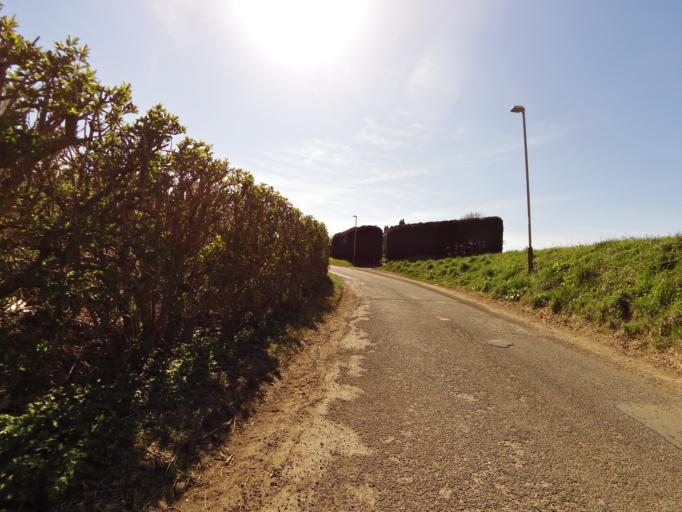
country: GB
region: Scotland
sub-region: Angus
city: Montrose
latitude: 56.6997
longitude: -2.4643
